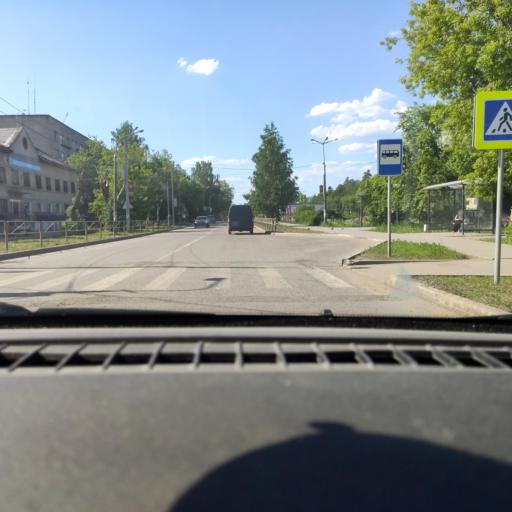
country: RU
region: Perm
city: Krasnokamsk
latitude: 58.0804
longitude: 55.7592
